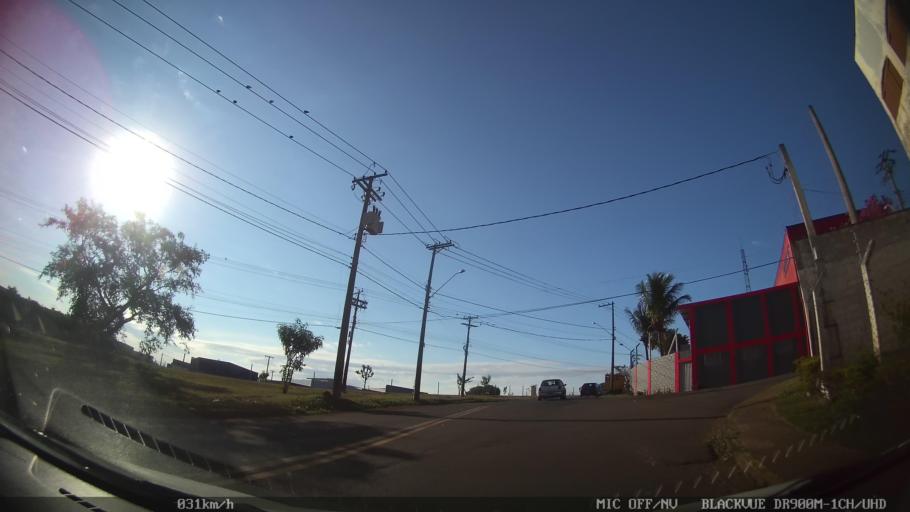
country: BR
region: Sao Paulo
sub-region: Piracicaba
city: Piracicaba
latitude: -22.6747
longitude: -47.6305
